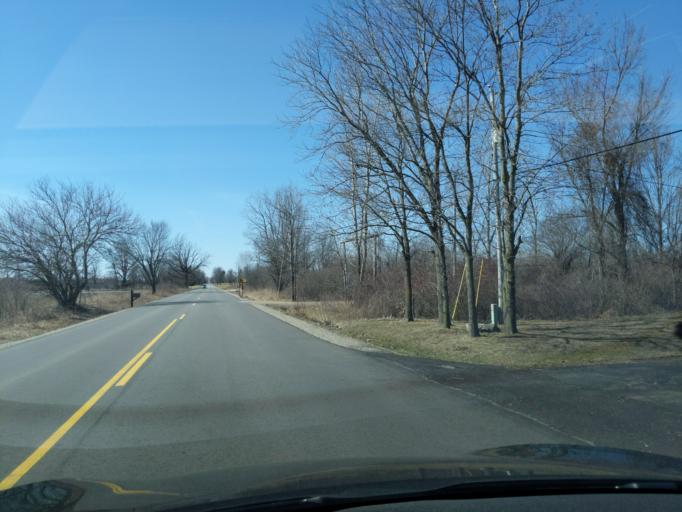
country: US
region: Michigan
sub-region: Eaton County
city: Grand Ledge
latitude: 42.7265
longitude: -84.7952
